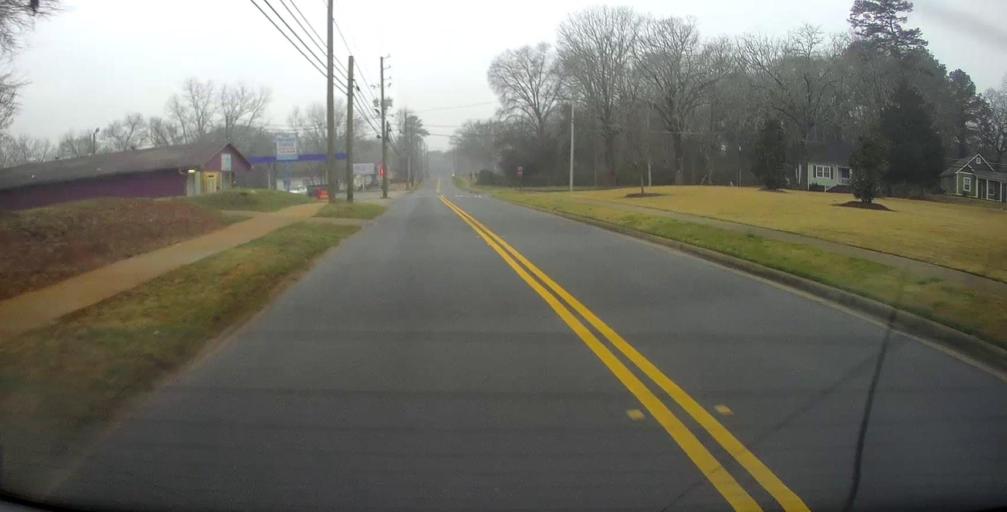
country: US
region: Georgia
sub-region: Spalding County
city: Griffin
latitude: 33.2419
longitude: -84.2767
